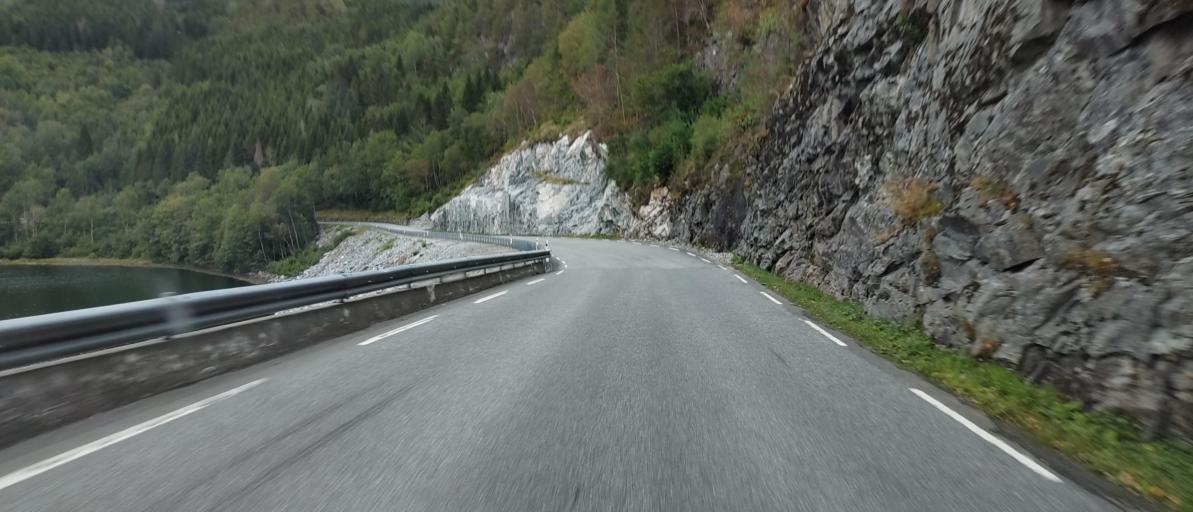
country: NO
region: More og Romsdal
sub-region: Rauma
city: Andalsnes
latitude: 62.5787
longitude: 7.5407
